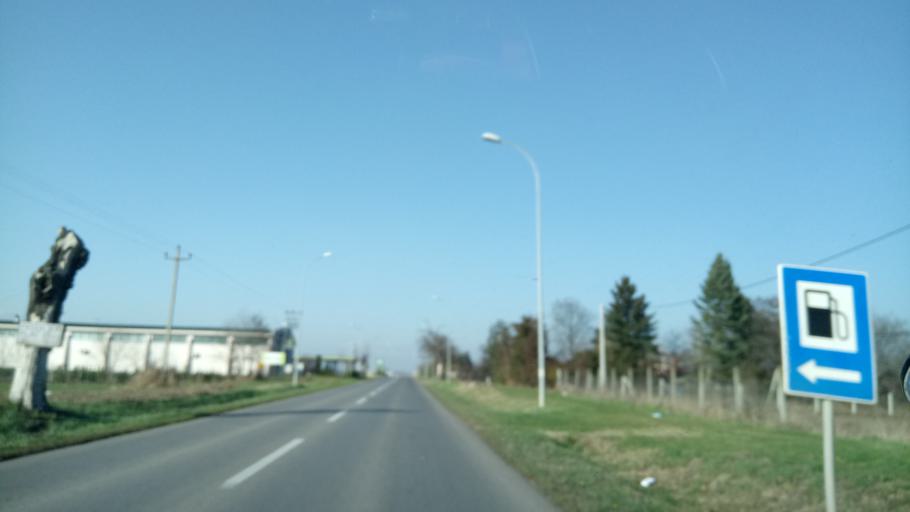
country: RS
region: Autonomna Pokrajina Vojvodina
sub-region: Sremski Okrug
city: Ingija
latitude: 45.0623
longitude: 20.0606
